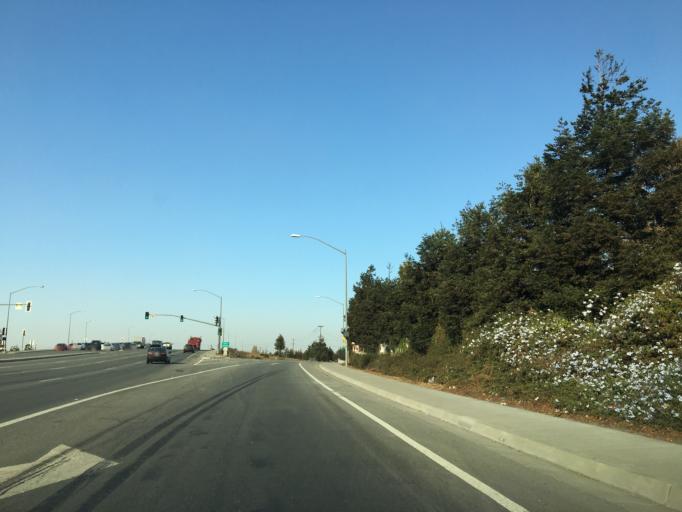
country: US
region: California
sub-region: Santa Clara County
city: Sunnyvale
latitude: 37.3888
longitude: -121.9958
